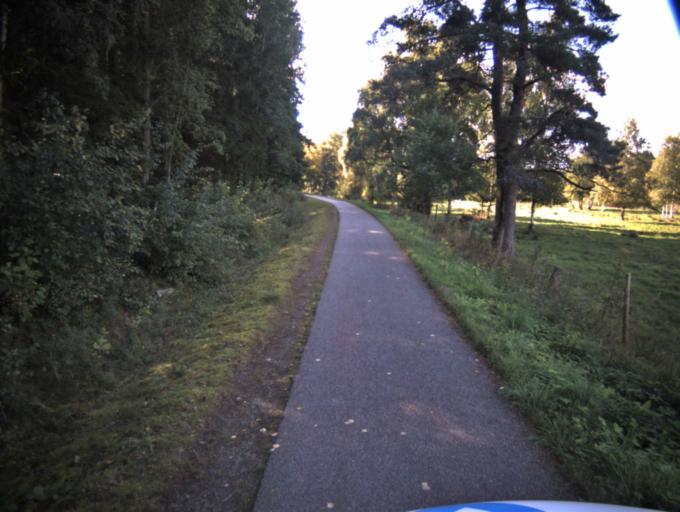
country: SE
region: Vaestra Goetaland
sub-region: Ulricehamns Kommun
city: Ulricehamn
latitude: 57.8397
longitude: 13.2728
